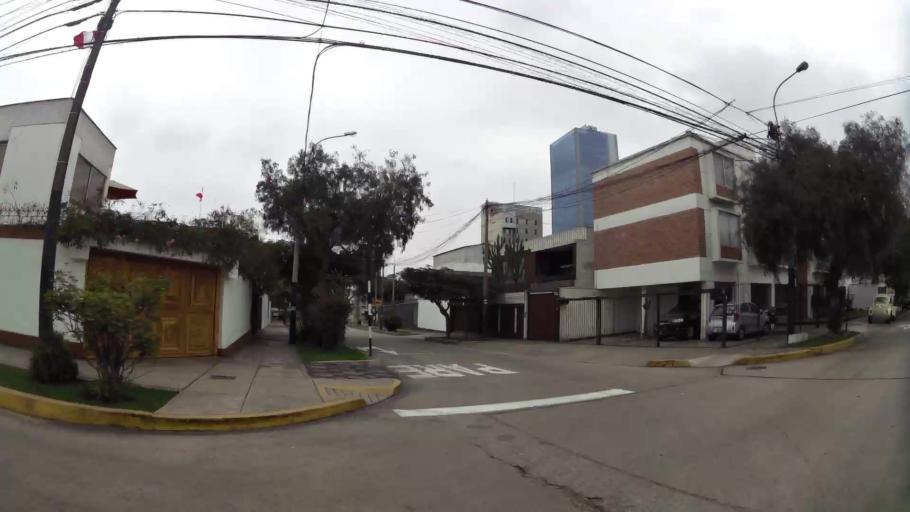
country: PE
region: Lima
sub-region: Lima
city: San Luis
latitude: -12.1002
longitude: -77.0172
